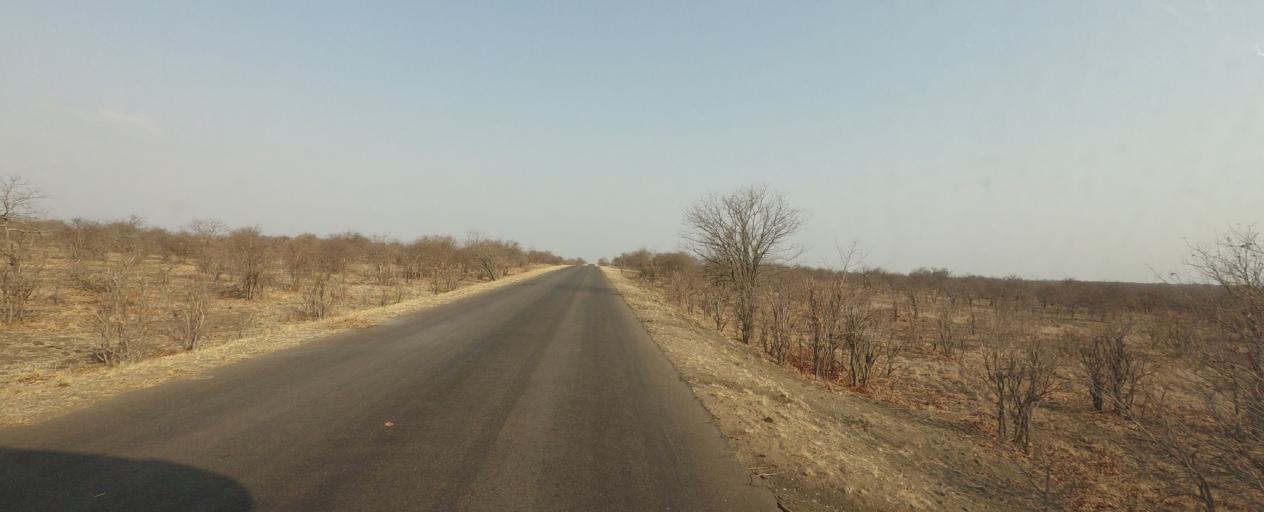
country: ZA
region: Limpopo
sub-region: Mopani District Municipality
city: Giyani
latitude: -23.0832
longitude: 31.4189
